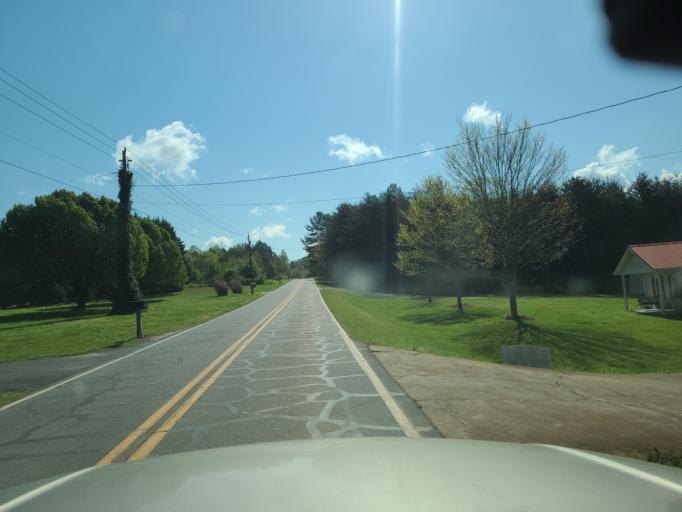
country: US
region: North Carolina
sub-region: Rutherford County
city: Spindale
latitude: 35.2961
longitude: -81.9583
